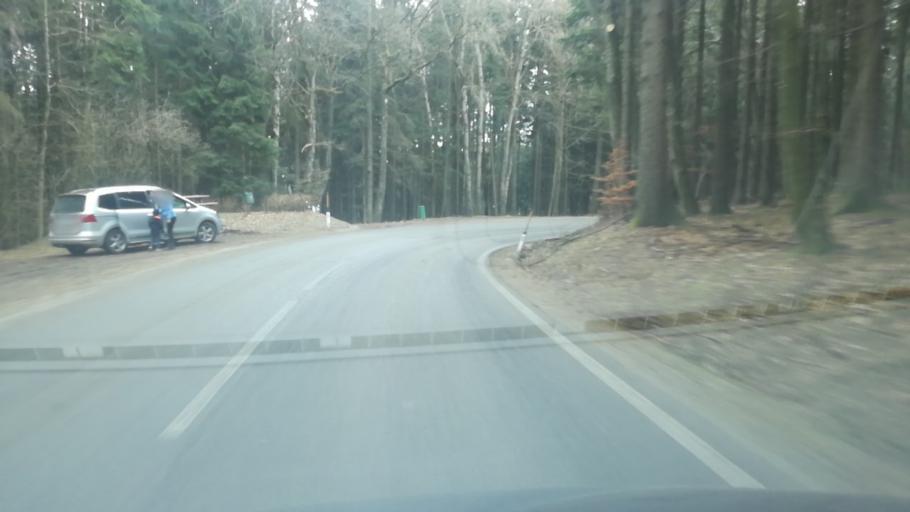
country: AT
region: Upper Austria
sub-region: Politischer Bezirk Vocklabruck
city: Frankenburg
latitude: 48.1137
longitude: 13.4795
